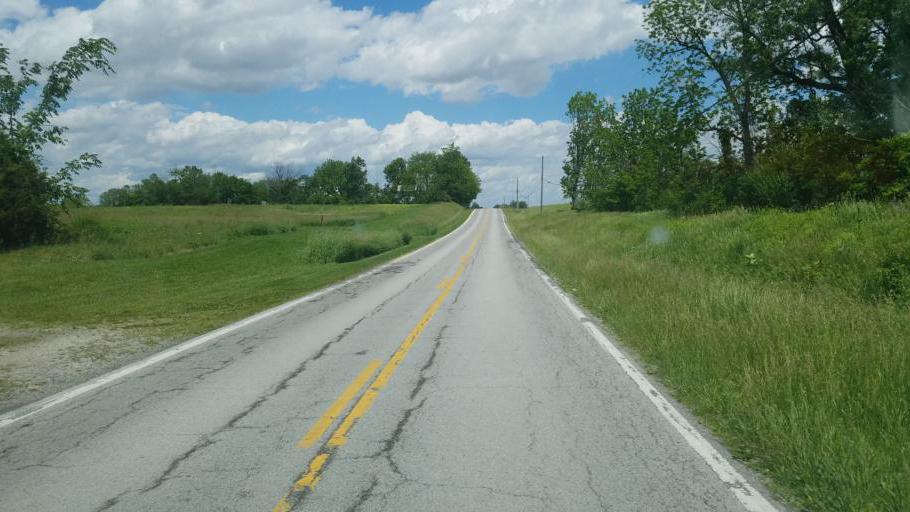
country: US
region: Ohio
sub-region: Huron County
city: Willard
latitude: 41.0867
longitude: -82.6846
